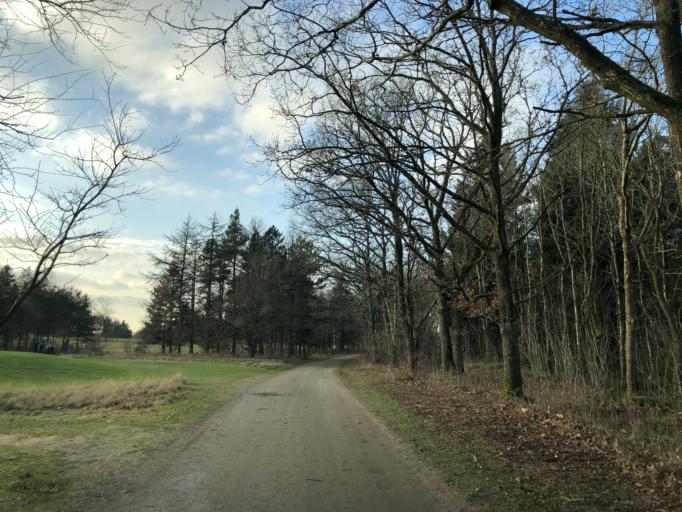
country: DK
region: Central Jutland
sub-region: Holstebro Kommune
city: Ulfborg
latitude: 56.3212
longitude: 8.4334
